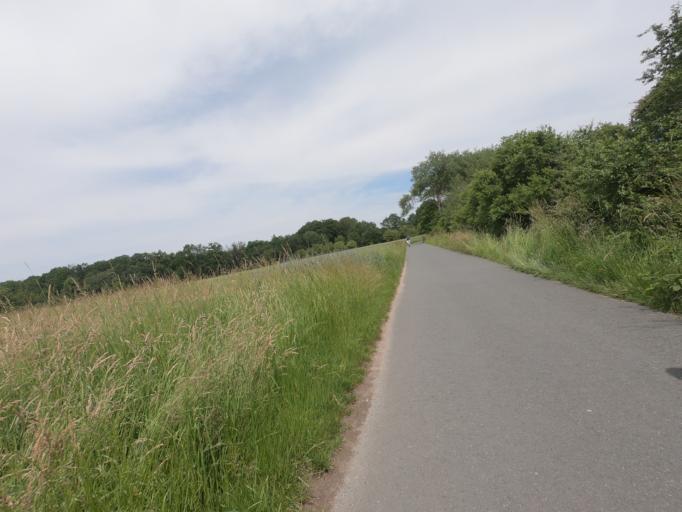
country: DE
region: Hesse
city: Langen
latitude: 50.0048
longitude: 8.6657
